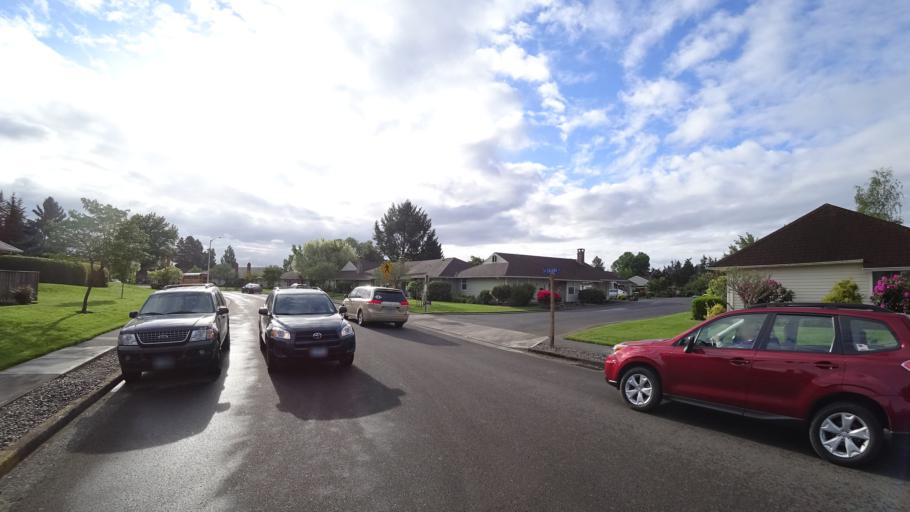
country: US
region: Oregon
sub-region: Washington County
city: Beaverton
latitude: 45.4822
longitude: -122.8244
